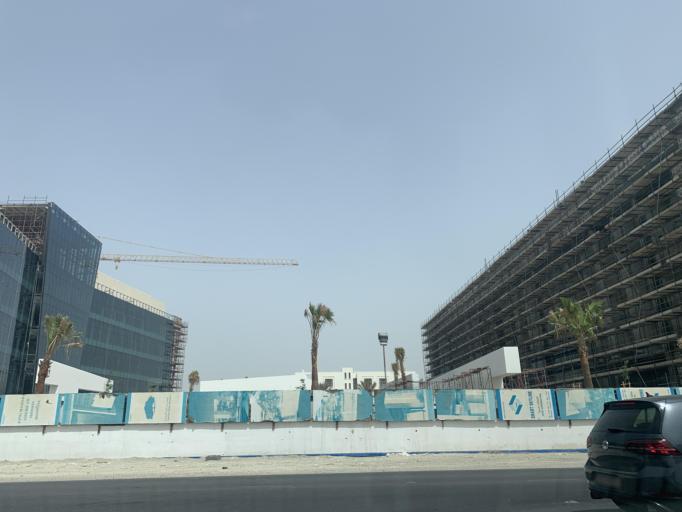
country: BH
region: Northern
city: Madinat `Isa
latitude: 26.1568
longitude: 50.5257
